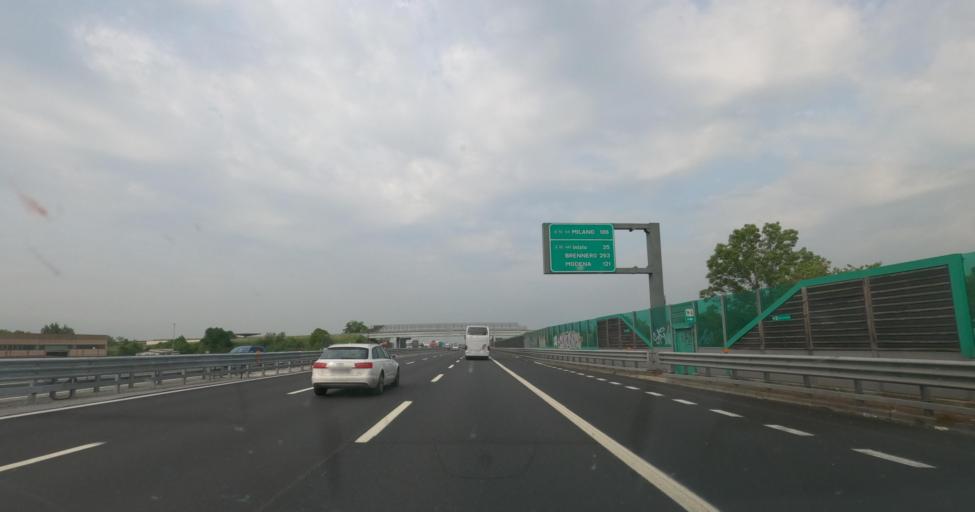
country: IT
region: Veneto
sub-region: Provincia di Verona
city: Locara
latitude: 45.4329
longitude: 11.3477
